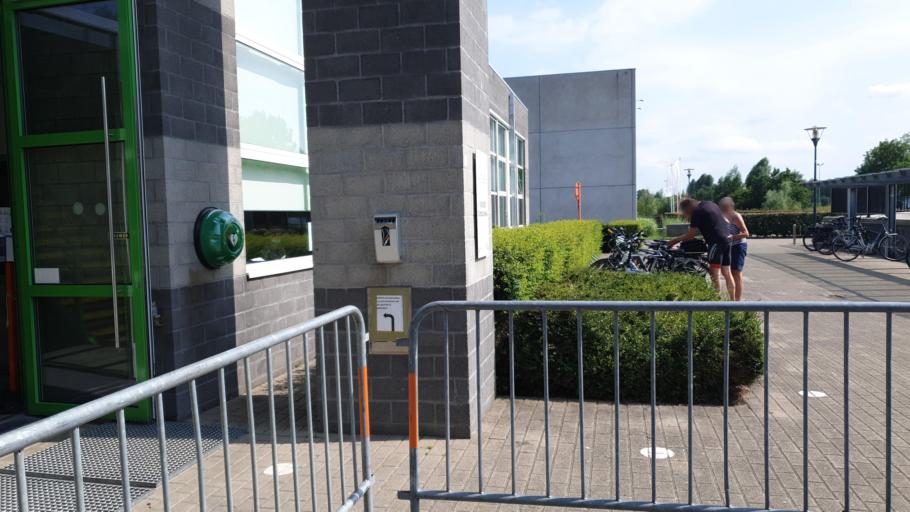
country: BE
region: Flanders
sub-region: Provincie West-Vlaanderen
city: Veurne
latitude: 51.1160
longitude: 2.6882
